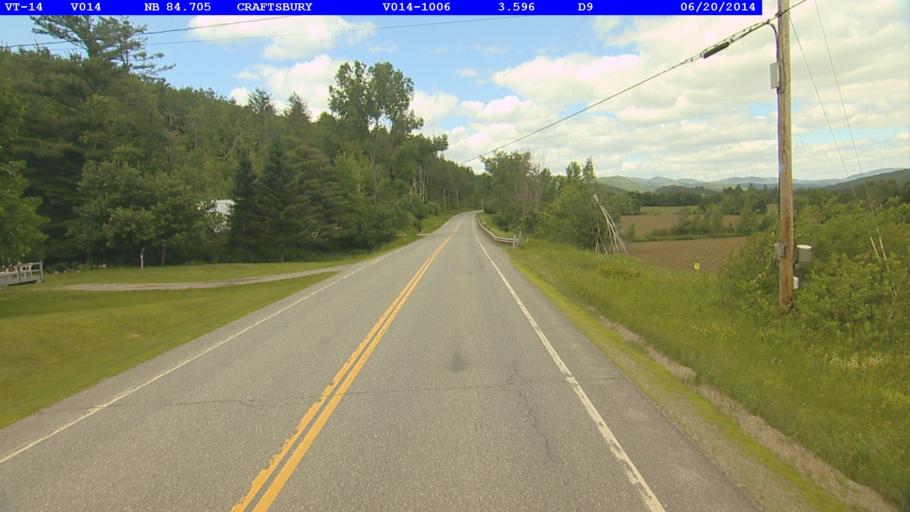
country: US
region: Vermont
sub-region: Caledonia County
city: Hardwick
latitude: 44.6429
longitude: -72.4019
